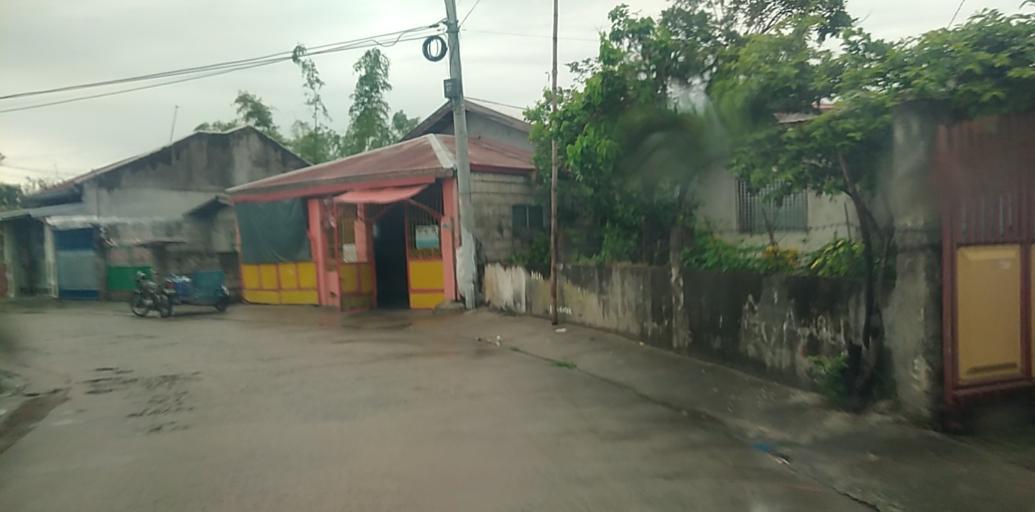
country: PH
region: Central Luzon
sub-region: Province of Pampanga
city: Arayat
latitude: 15.1359
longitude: 120.7418
